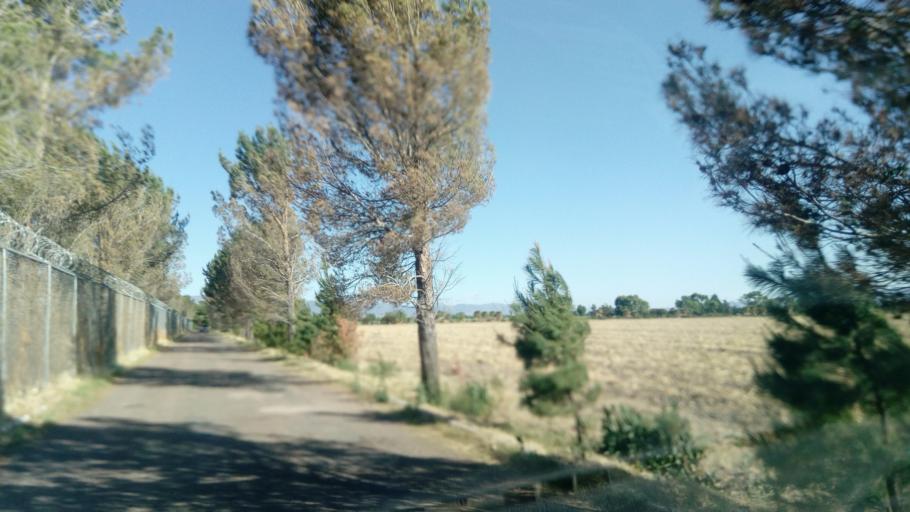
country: MX
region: Durango
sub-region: Durango
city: Jose Refugio Salcido
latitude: 24.0105
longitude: -104.5505
